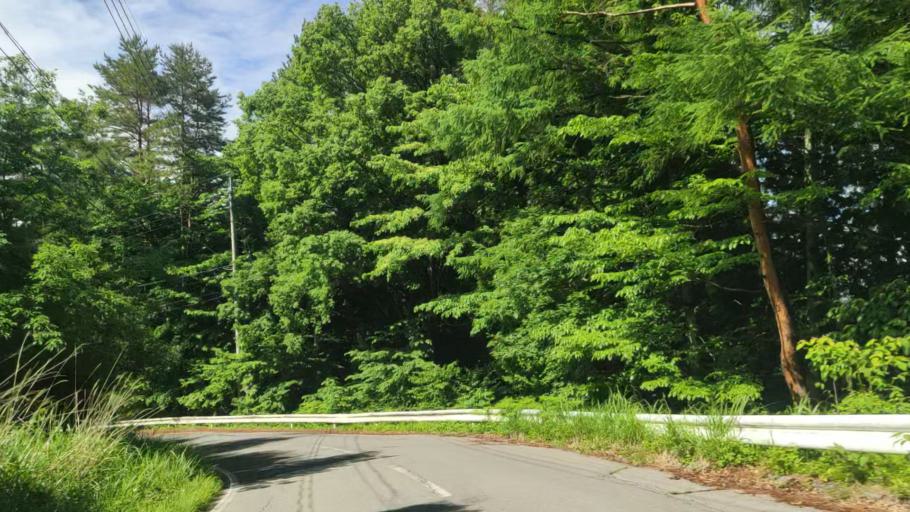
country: JP
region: Nagano
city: Suwa
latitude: 36.0727
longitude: 138.1373
